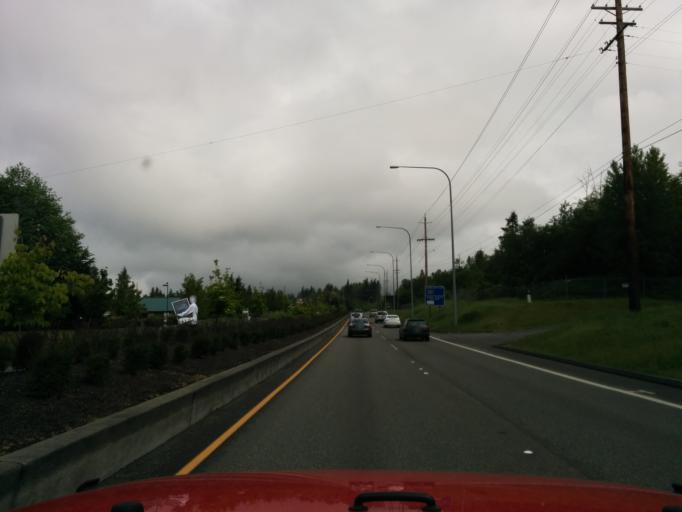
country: US
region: Washington
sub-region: Snohomish County
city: Mukilteo
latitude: 47.9064
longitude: -122.2930
